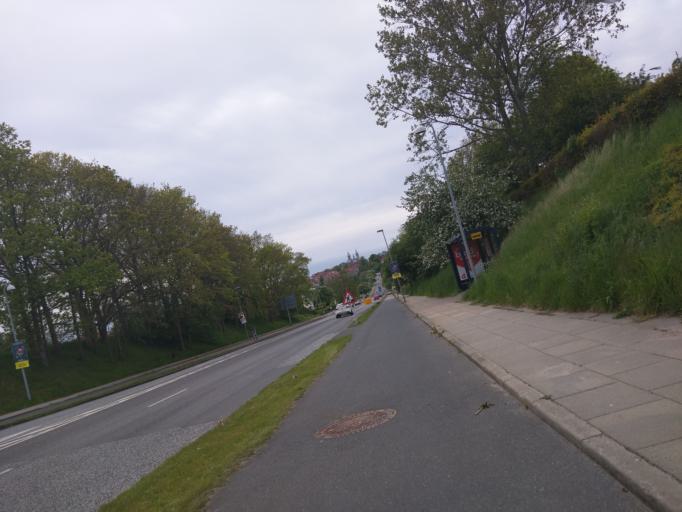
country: DK
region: Central Jutland
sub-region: Viborg Kommune
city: Viborg
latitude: 56.4490
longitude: 9.4297
